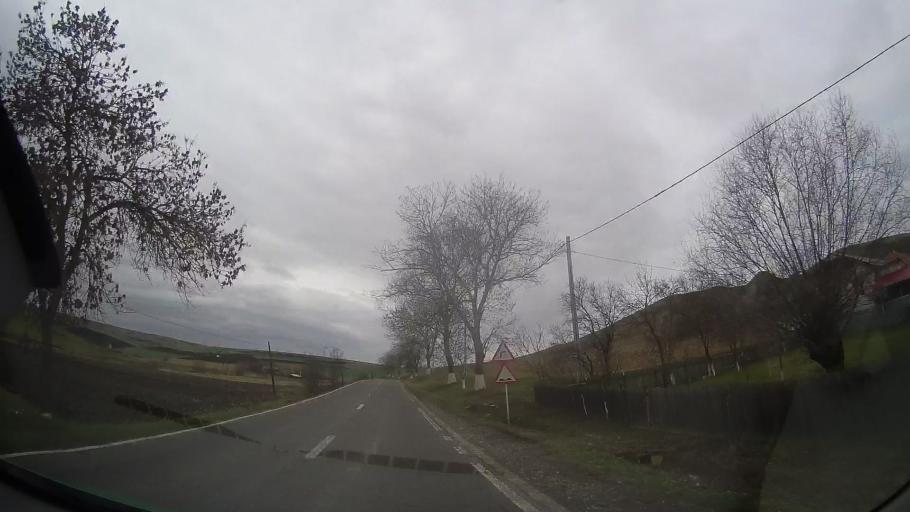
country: RO
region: Bistrita-Nasaud
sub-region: Comuna Urmenis
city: Urmenis
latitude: 46.7611
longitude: 24.3887
